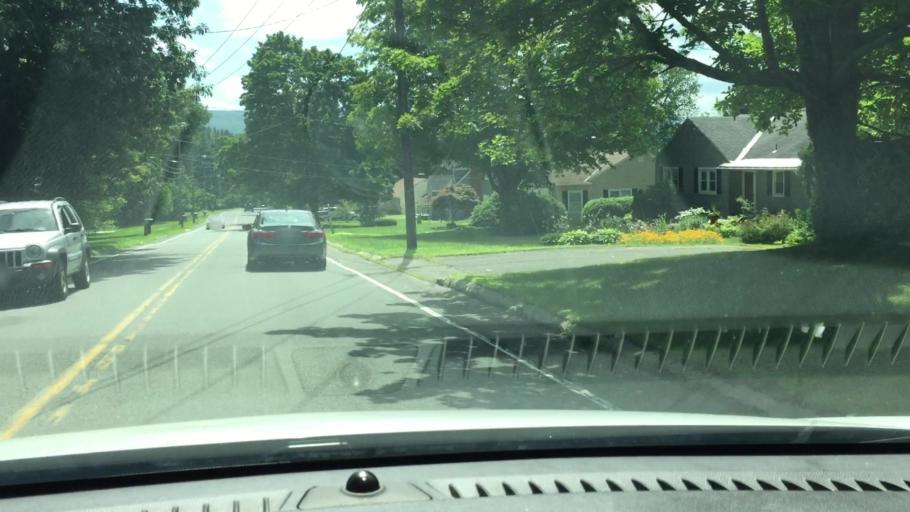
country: US
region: Massachusetts
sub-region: Berkshire County
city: Pittsfield
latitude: 42.4748
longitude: -73.2175
